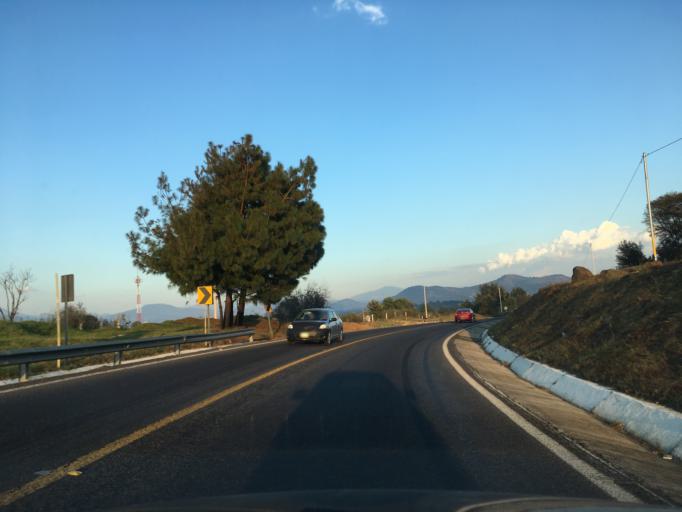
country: MX
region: Michoacan
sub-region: Patzcuaro
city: Santa Ana Chapitiro
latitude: 19.5223
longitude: -101.6618
